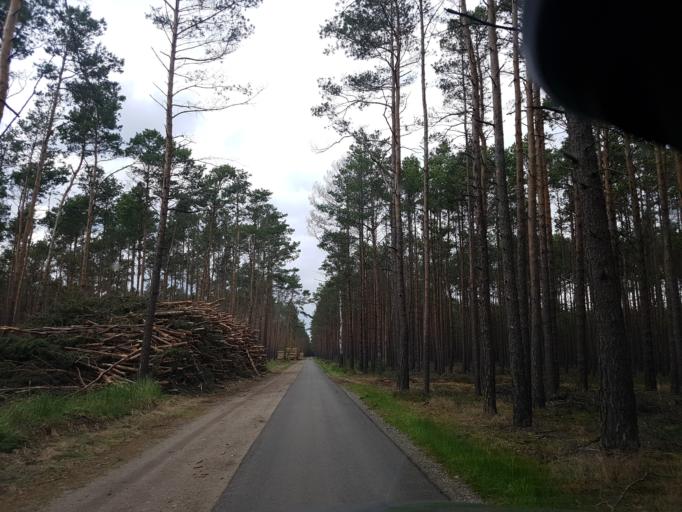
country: DE
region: Brandenburg
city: Crinitz
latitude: 51.6762
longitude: 13.7810
